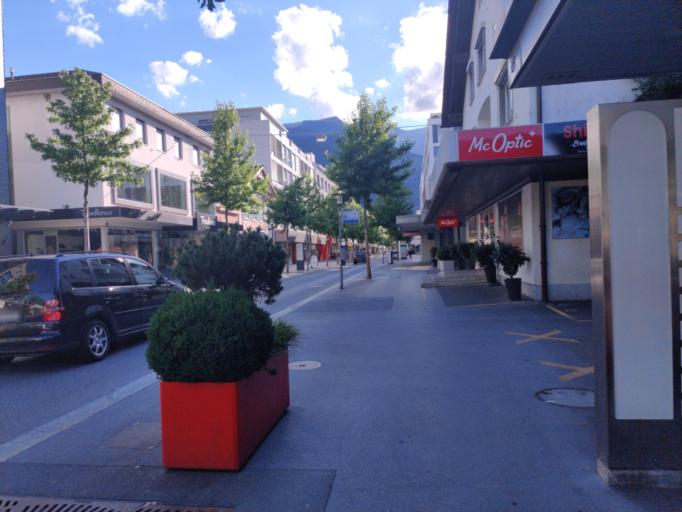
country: CH
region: Saint Gallen
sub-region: Wahlkreis Werdenberg
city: Buchs
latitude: 47.1669
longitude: 9.4771
